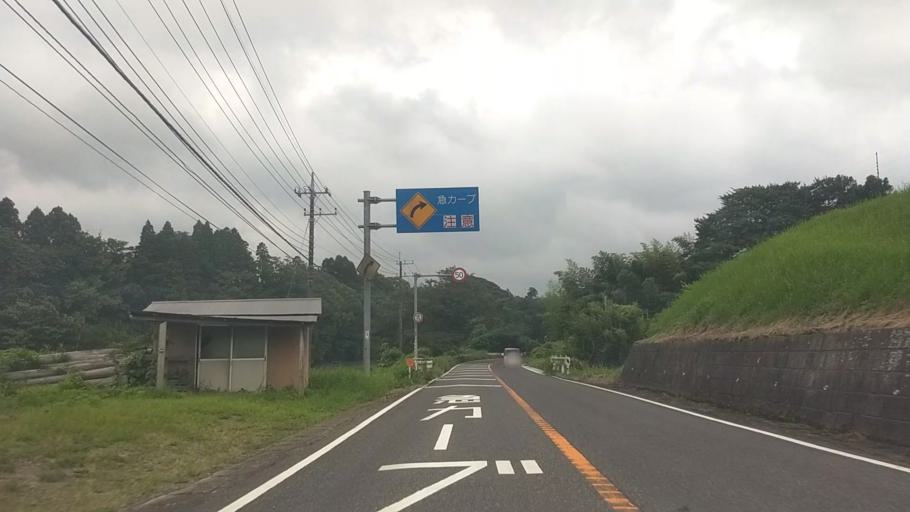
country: JP
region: Chiba
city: Kawaguchi
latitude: 35.2403
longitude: 140.0745
